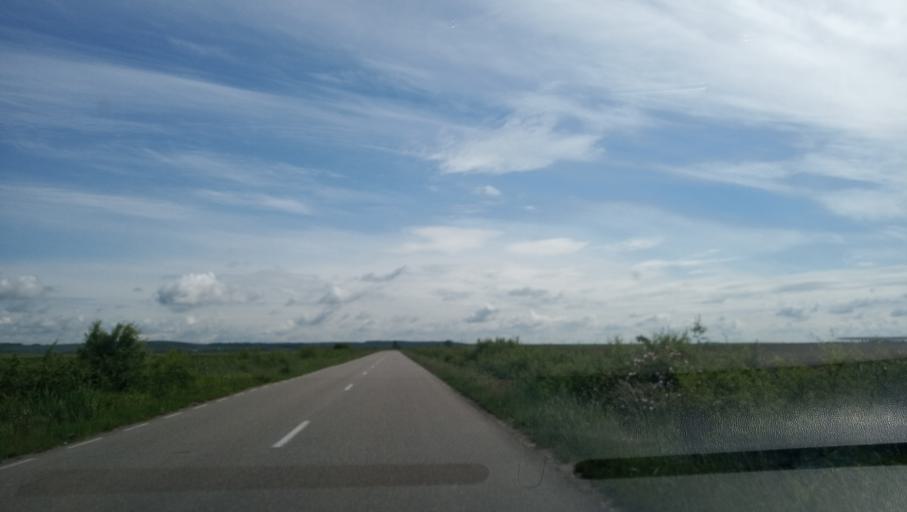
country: RO
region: Timis
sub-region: Comuna Topolovatu Mare
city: Topolovatu Mare
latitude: 45.7838
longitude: 21.6427
